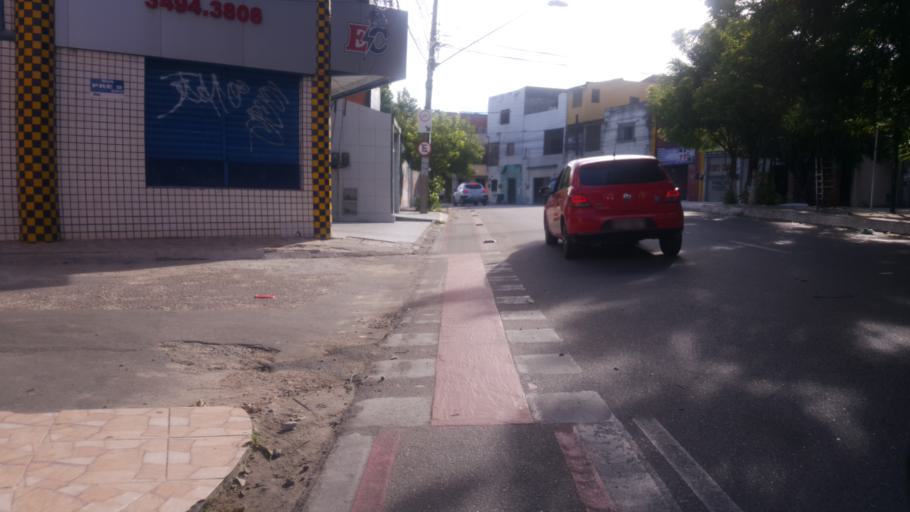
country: BR
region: Ceara
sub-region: Fortaleza
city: Fortaleza
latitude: -3.7549
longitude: -38.5405
